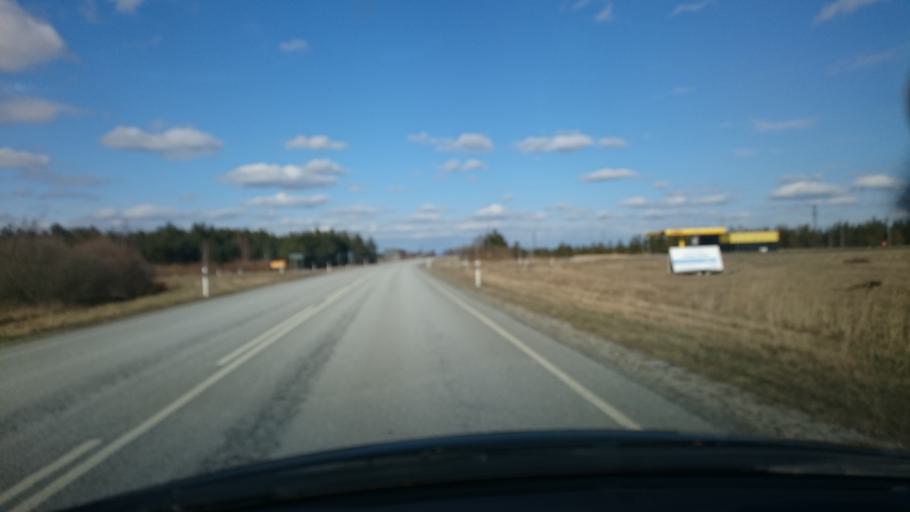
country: EE
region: Laeaene
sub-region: Lihula vald
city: Lihula
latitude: 58.6972
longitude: 23.8258
